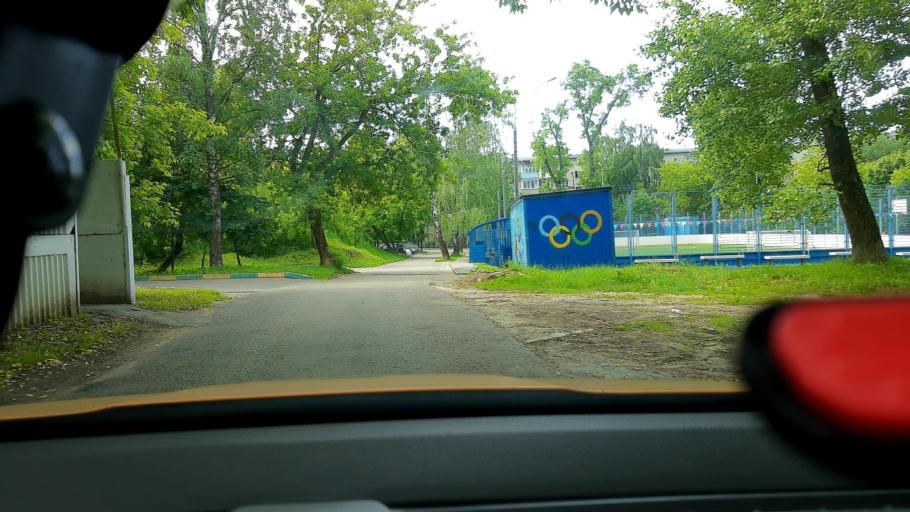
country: RU
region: Moscow
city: Zhulebino
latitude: 55.7195
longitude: 37.8644
